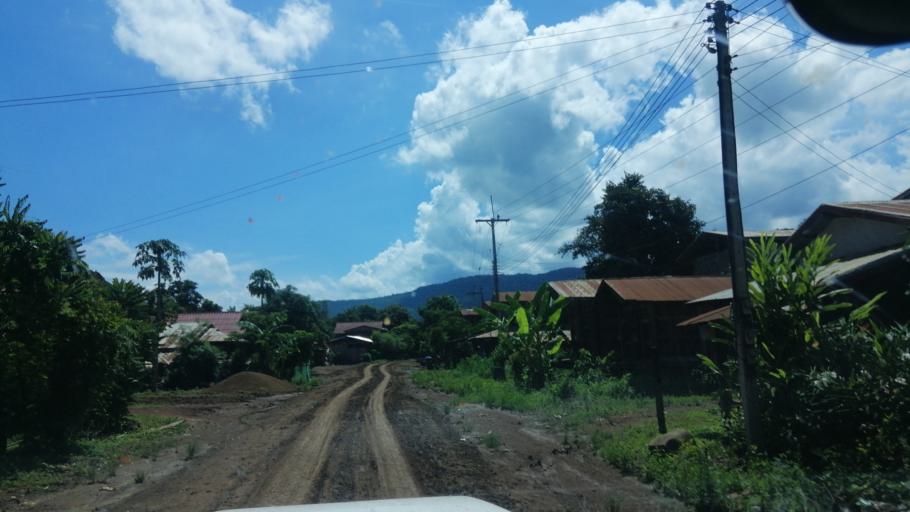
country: TH
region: Uttaradit
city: Ban Khok
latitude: 18.1005
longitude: 101.2545
